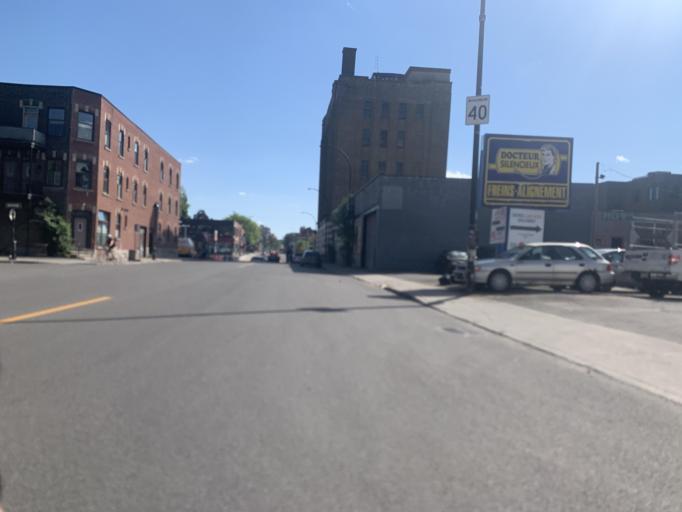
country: CA
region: Quebec
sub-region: Montreal
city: Montreal
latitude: 45.5267
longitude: -73.6094
